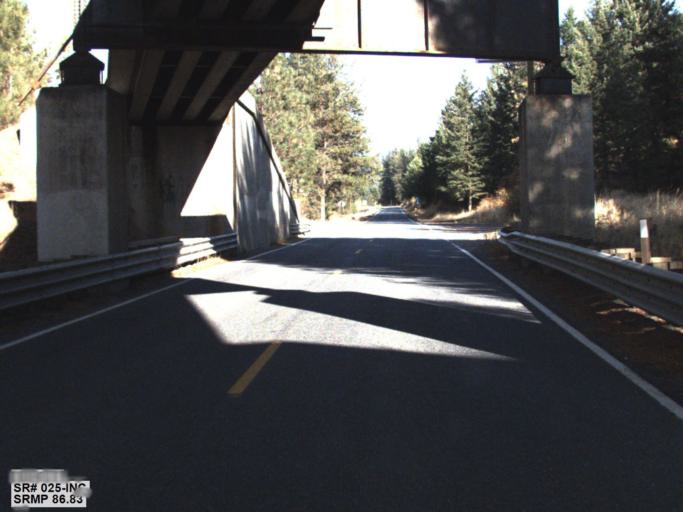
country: US
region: Washington
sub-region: Stevens County
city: Kettle Falls
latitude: 48.6665
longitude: -118.0492
